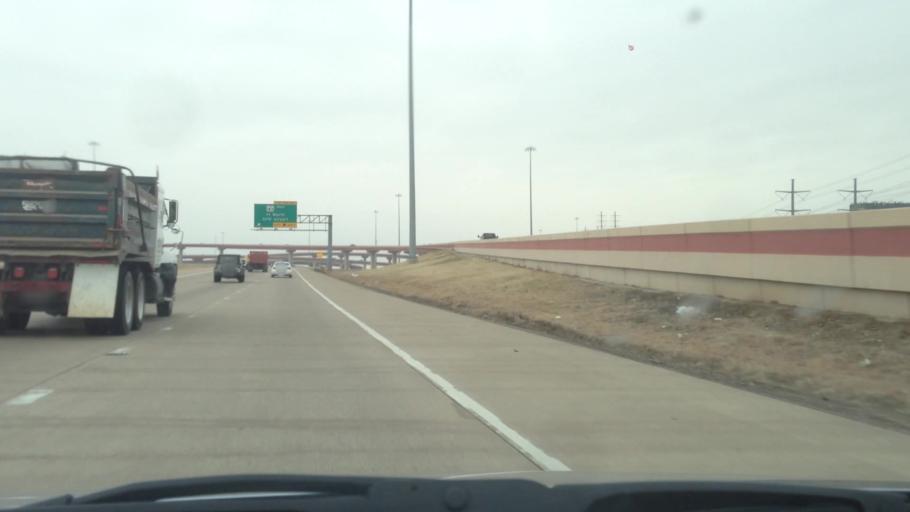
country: US
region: Texas
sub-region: Tarrant County
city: Euless
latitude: 32.8445
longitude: -97.0171
